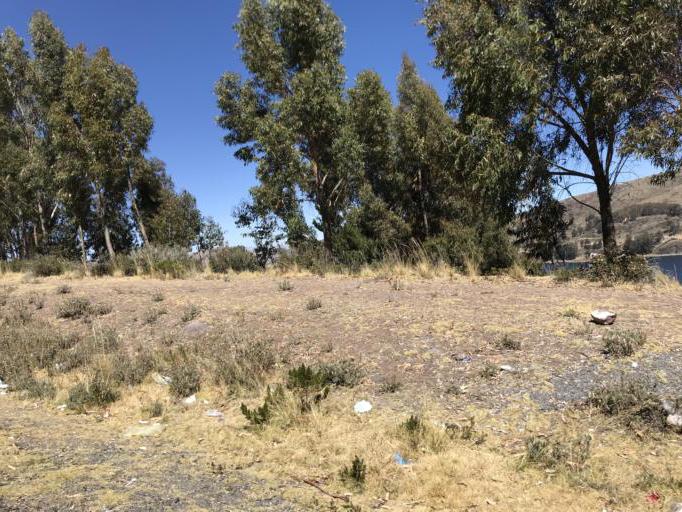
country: BO
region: La Paz
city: San Pablo
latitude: -16.2181
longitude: -68.8363
